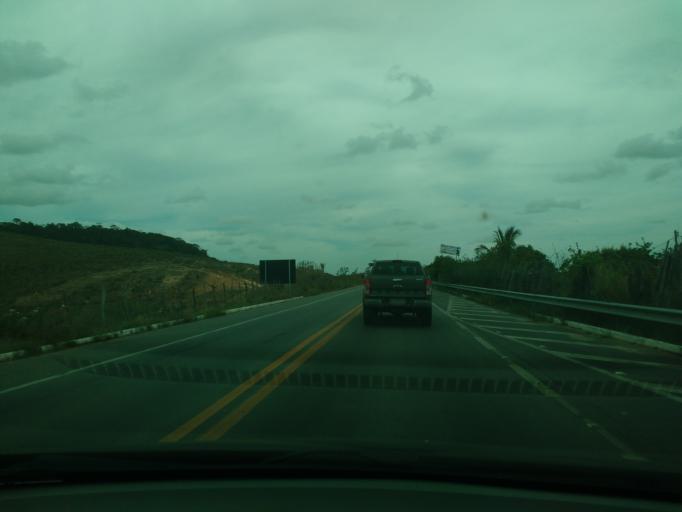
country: BR
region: Alagoas
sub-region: Murici
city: Murici
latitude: -9.3166
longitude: -35.9301
